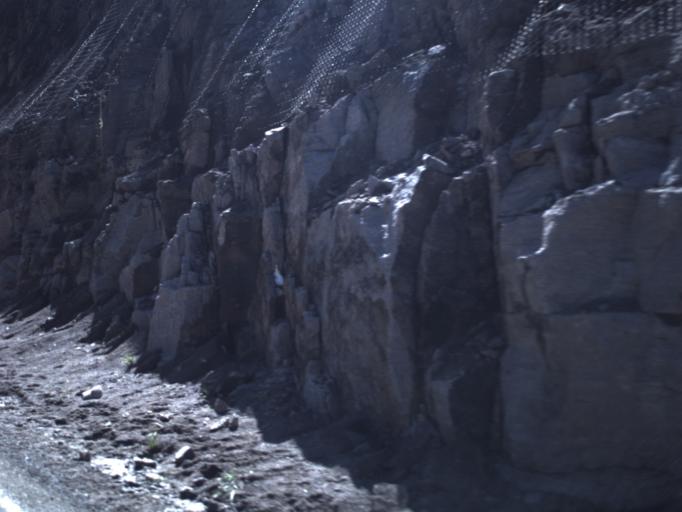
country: US
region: Utah
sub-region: Beaver County
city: Beaver
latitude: 38.2884
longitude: -112.4447
